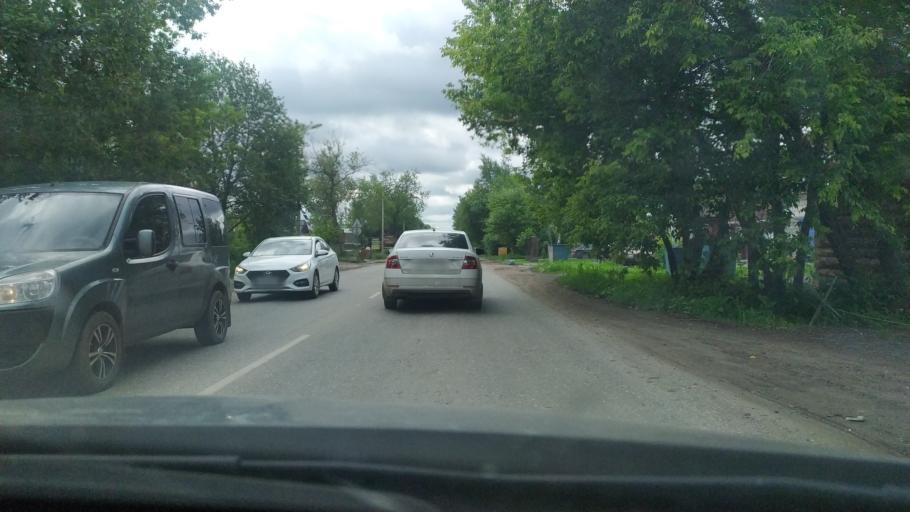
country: RU
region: Perm
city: Perm
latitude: 57.9811
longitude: 56.3049
